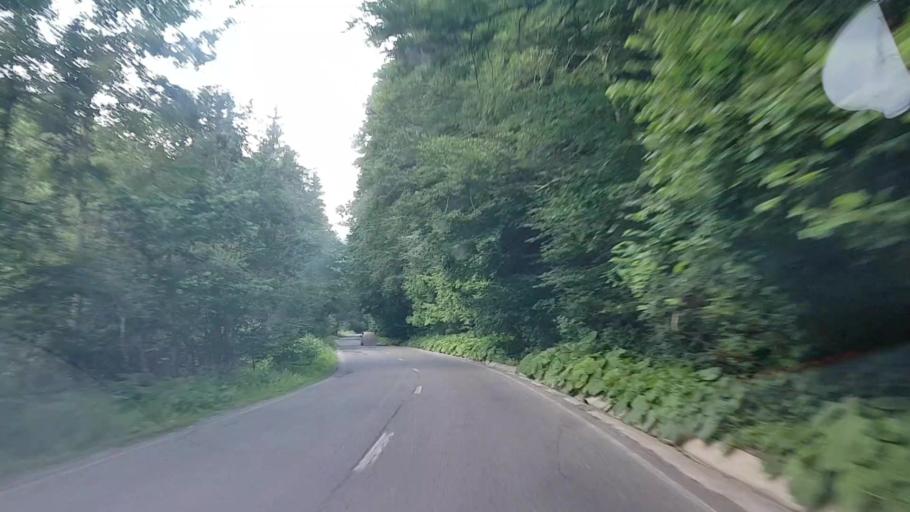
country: RO
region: Harghita
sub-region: Comuna Praid
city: Ocna de Sus
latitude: 46.6065
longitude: 25.2402
